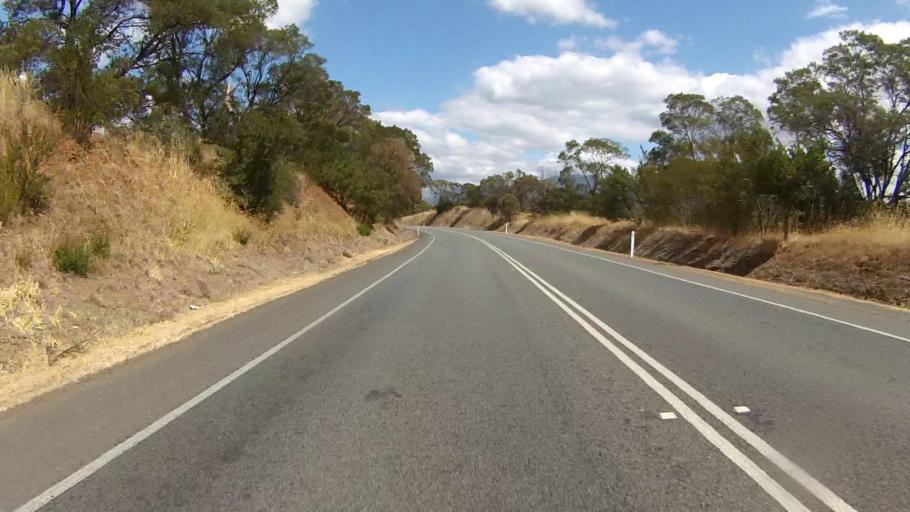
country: AU
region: Tasmania
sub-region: Brighton
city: Old Beach
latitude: -42.7554
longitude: 147.2696
